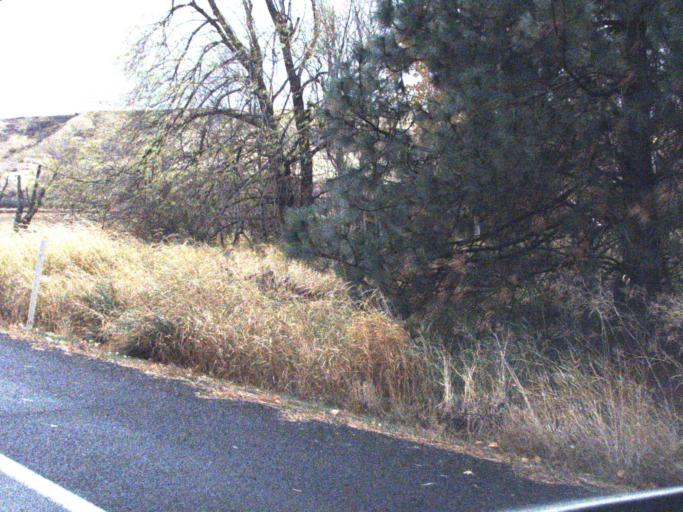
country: US
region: Washington
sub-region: Walla Walla County
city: Waitsburg
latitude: 46.2871
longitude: -118.0704
